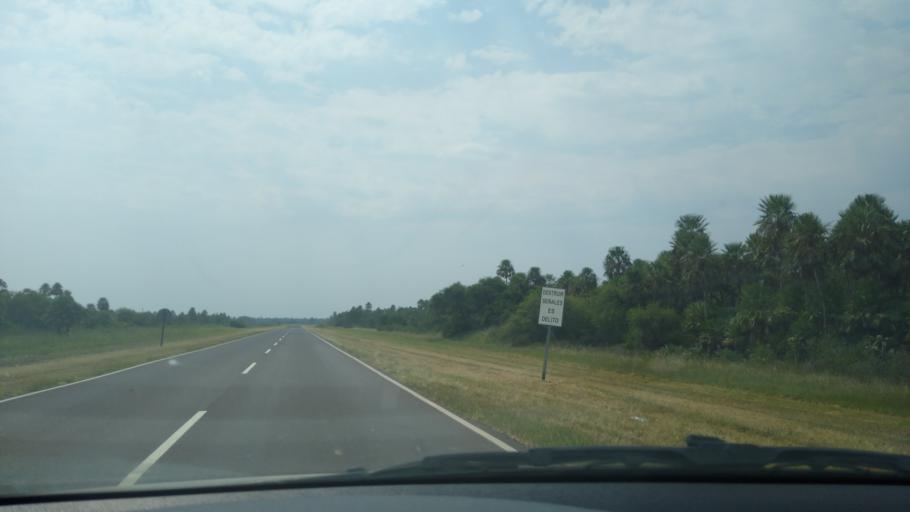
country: AR
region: Chaco
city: Margarita Belen
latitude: -27.0791
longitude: -58.9608
